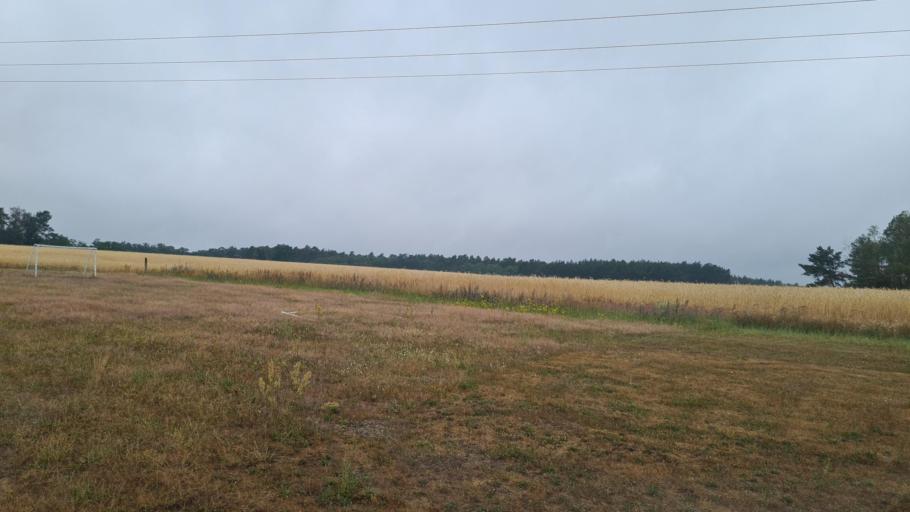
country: DE
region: Brandenburg
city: Ludwigsfelde
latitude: 52.2751
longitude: 13.2761
